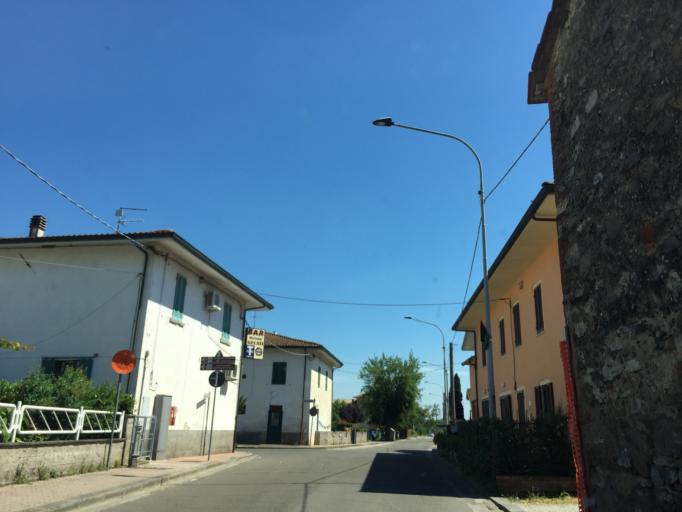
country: IT
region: Tuscany
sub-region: Provincia di Pistoia
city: Anchione
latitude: 43.8218
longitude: 10.7599
